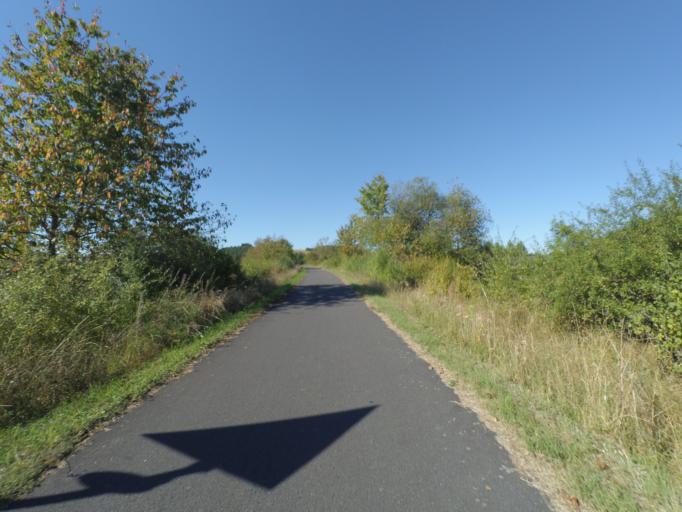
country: DE
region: Rheinland-Pfalz
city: Mehren
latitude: 50.1589
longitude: 6.8786
